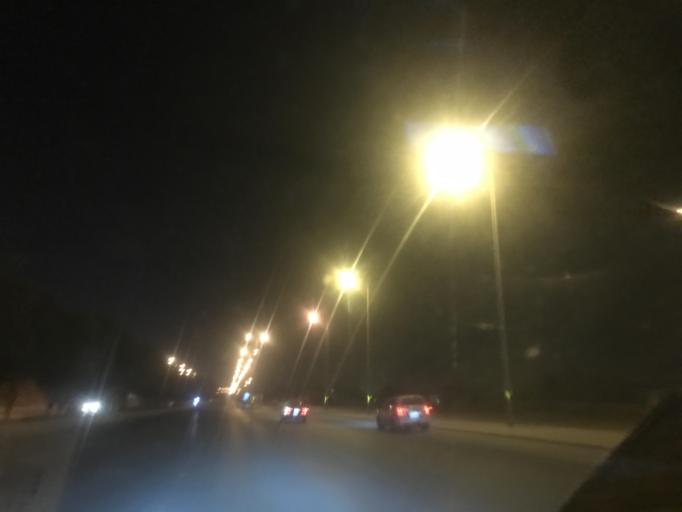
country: SA
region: Ar Riyad
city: Riyadh
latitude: 24.7944
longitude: 46.5867
